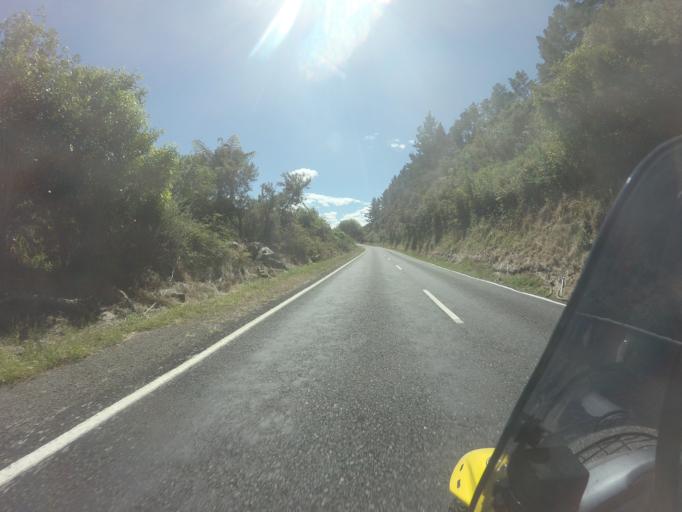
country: NZ
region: Bay of Plenty
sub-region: Kawerau District
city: Kawerau
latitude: -38.2665
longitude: 176.8203
